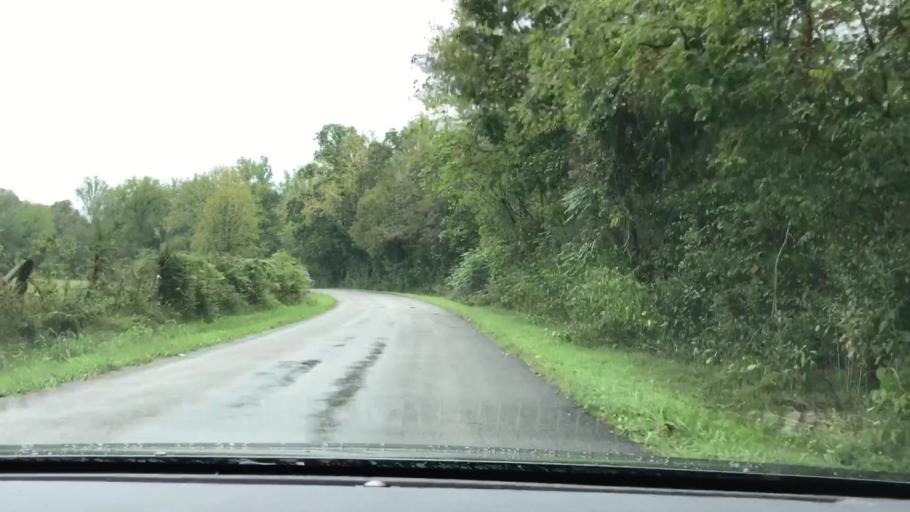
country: US
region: Tennessee
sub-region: Macon County
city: Red Boiling Springs
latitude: 36.5902
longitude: -85.7775
